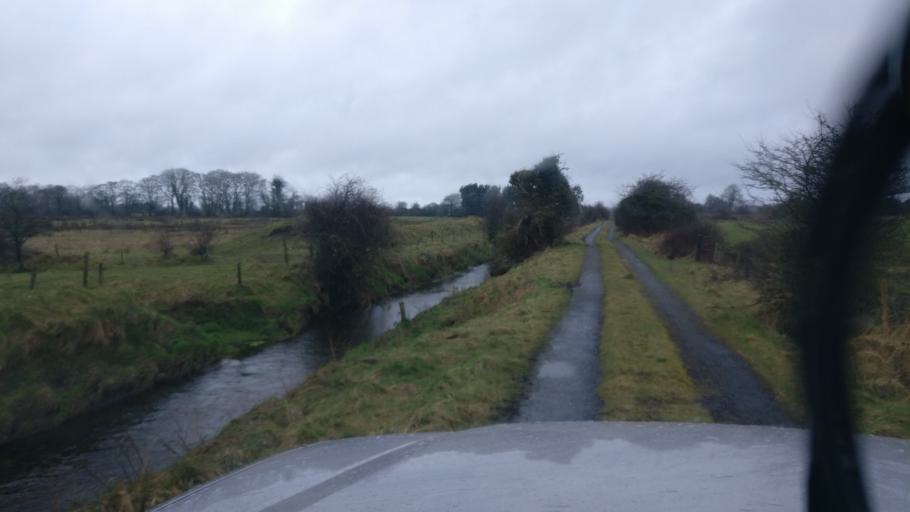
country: IE
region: Connaught
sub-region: County Galway
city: Ballinasloe
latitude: 53.2436
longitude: -8.3384
